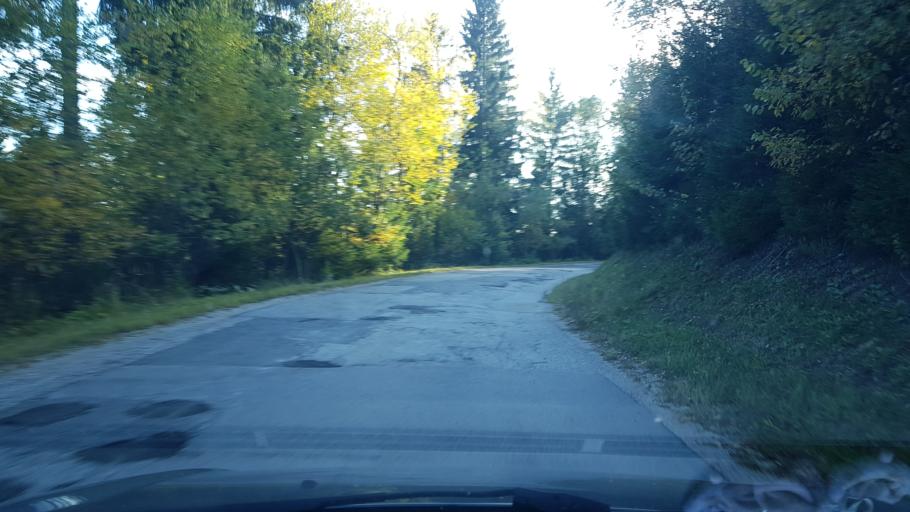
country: SI
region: Slovenj Gradec
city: Legen
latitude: 46.4912
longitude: 15.1805
